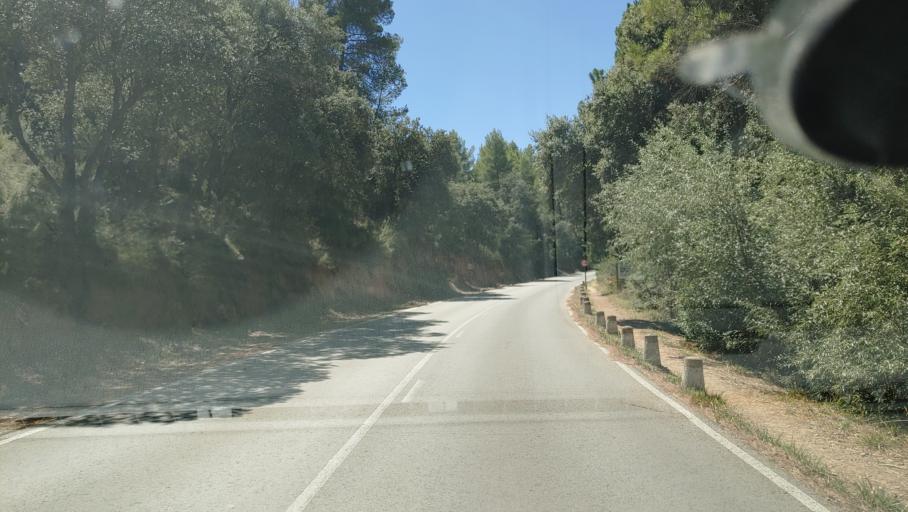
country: ES
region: Castille-La Mancha
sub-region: Provincia de Ciudad Real
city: Ruidera
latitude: 38.9537
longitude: -2.8615
